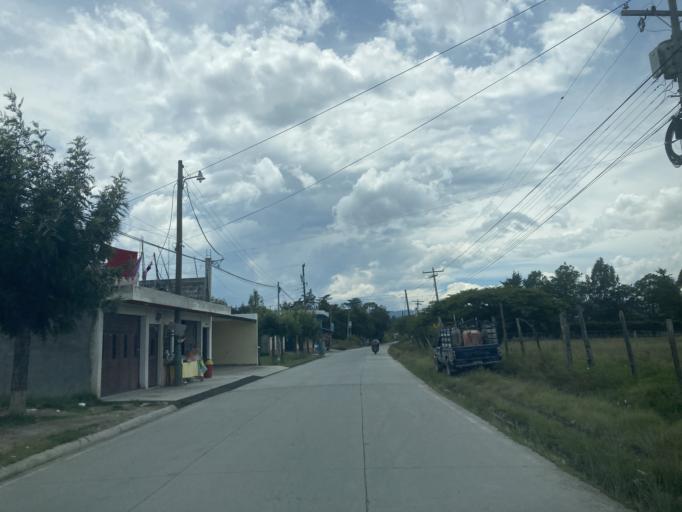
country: GT
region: Huehuetenango
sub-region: Municipio de Huehuetenango
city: Huehuetenango
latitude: 15.3305
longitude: -91.4894
